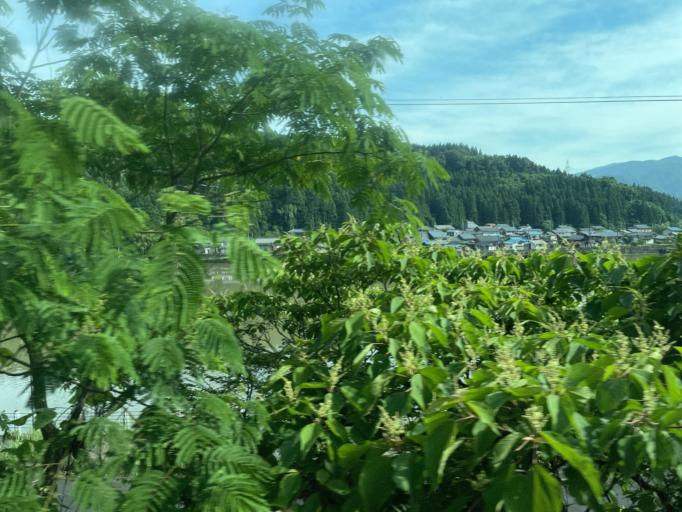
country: JP
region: Niigata
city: Suibara
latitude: 37.7036
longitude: 139.3984
